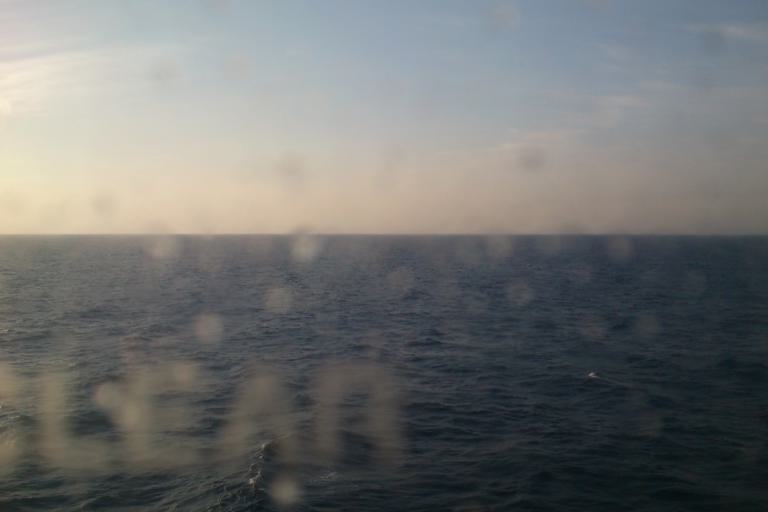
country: JP
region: Ishikawa
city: Nanao
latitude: 37.6908
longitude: 136.3706
